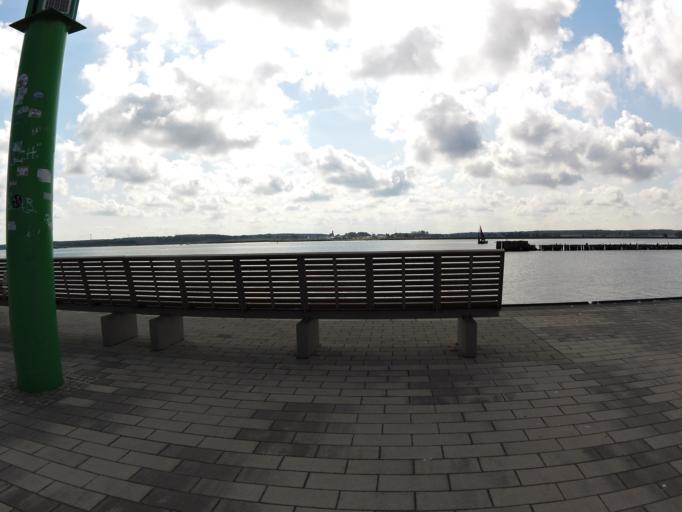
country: DE
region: Mecklenburg-Vorpommern
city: Kroslin
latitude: 54.1345
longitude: 13.7665
